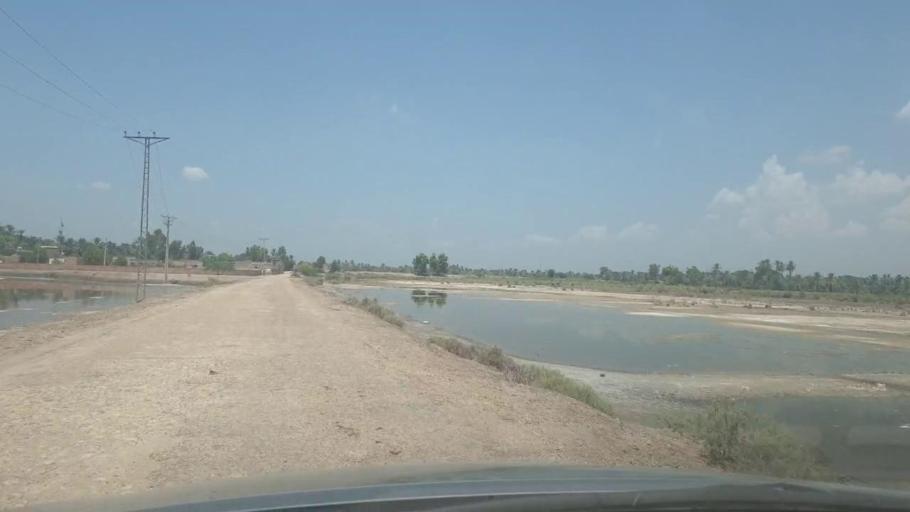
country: PK
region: Sindh
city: Kot Diji
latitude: 27.4184
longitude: 68.7362
